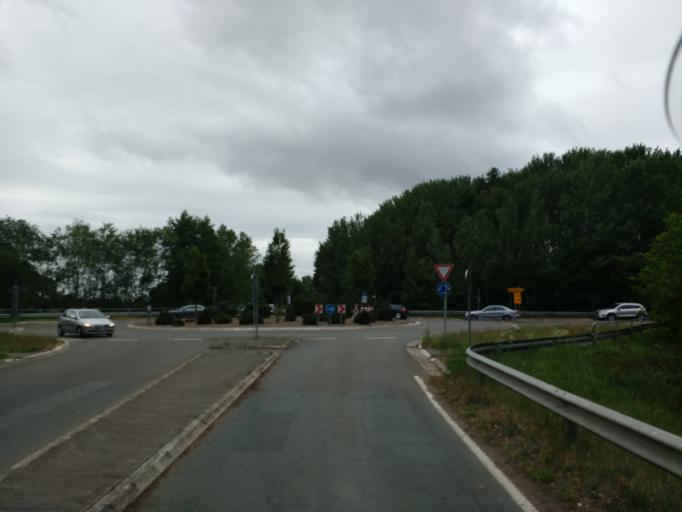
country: DE
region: Lower Saxony
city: Dinklage
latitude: 52.6376
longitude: 8.1523
